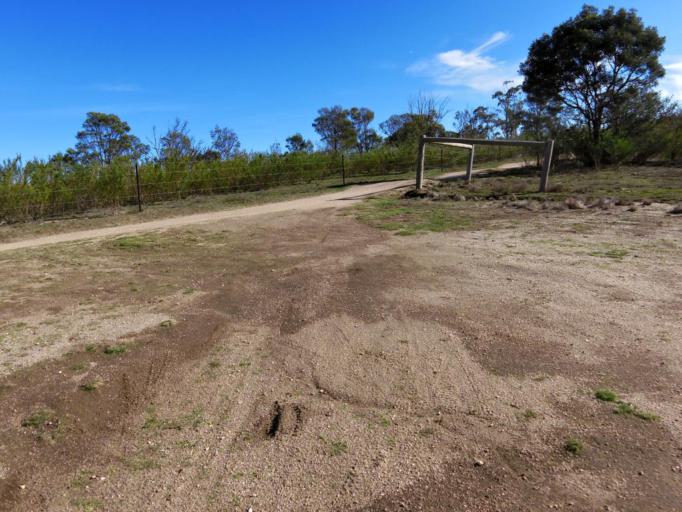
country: AU
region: Victoria
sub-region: Wyndham
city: Little River
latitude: -37.9340
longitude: 144.4344
